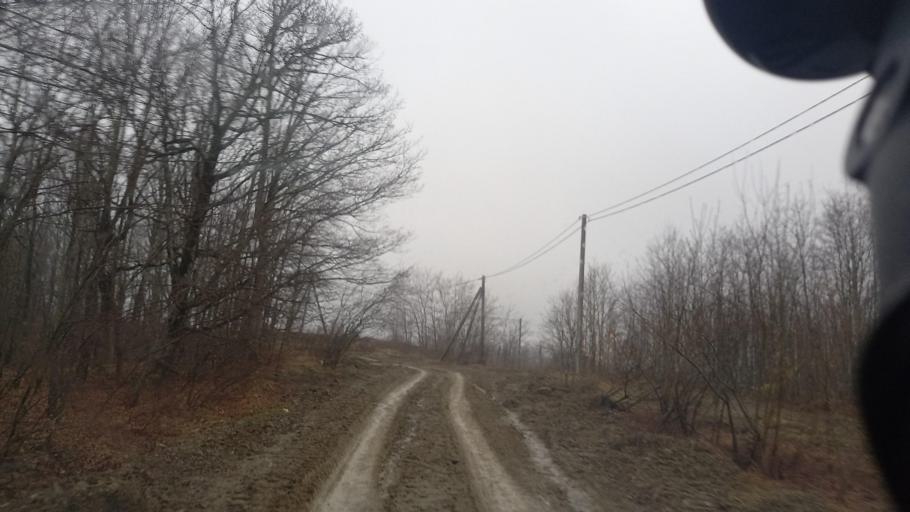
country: RU
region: Krasnodarskiy
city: Saratovskaya
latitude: 44.6190
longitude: 39.2376
